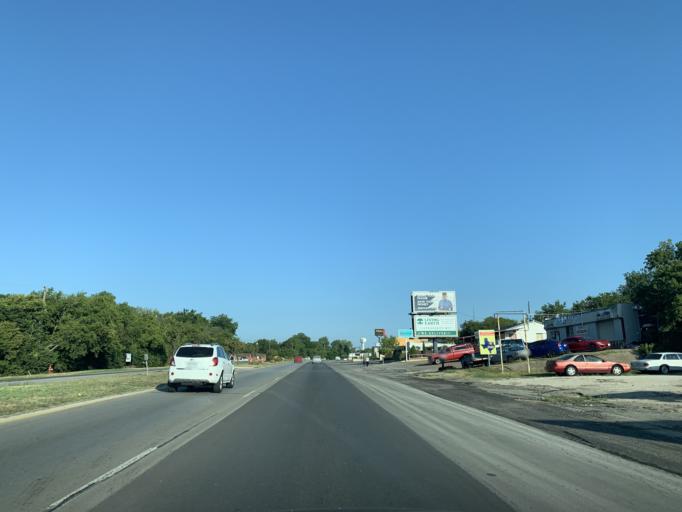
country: US
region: Texas
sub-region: Tarrant County
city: Sansom Park
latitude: 32.7970
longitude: -97.4011
